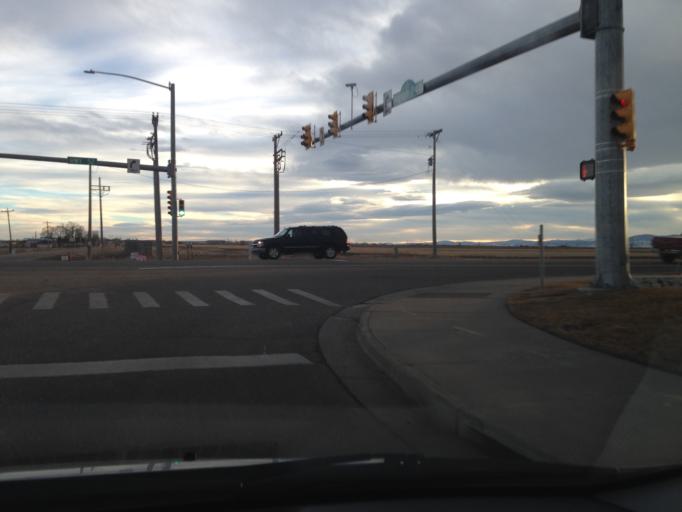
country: US
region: Colorado
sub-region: Weld County
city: Dacono
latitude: 40.0879
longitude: -104.9991
